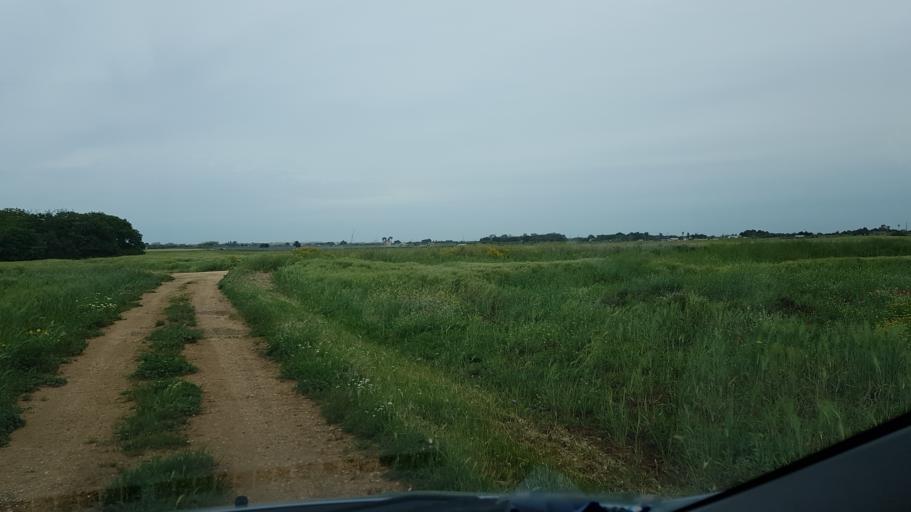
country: IT
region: Apulia
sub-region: Provincia di Brindisi
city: Brindisi
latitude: 40.6549
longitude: 17.8811
